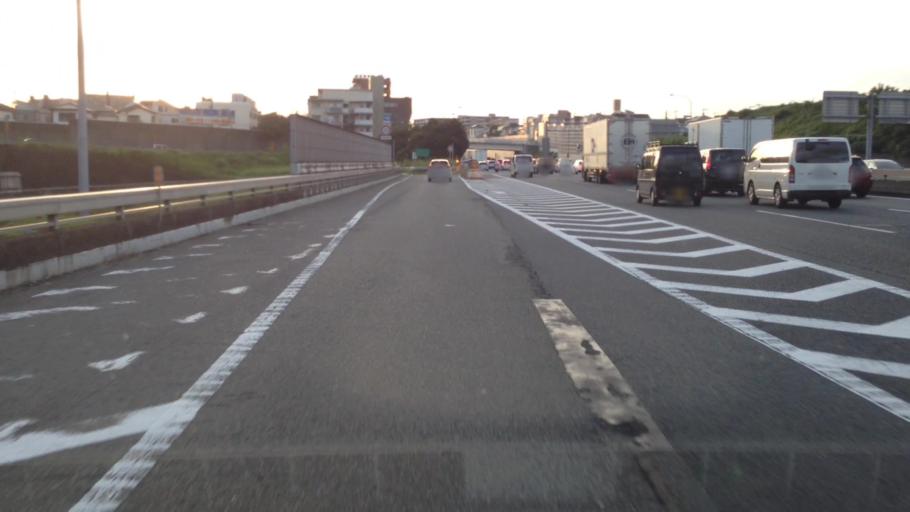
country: JP
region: Kanagawa
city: Yokohama
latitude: 35.4500
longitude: 139.5699
